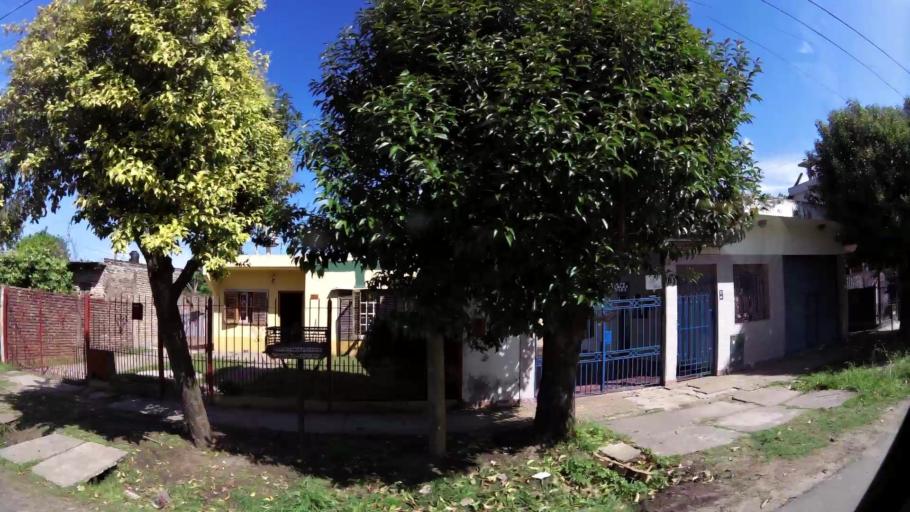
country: AR
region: Buenos Aires
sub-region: Partido de Quilmes
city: Quilmes
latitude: -34.8005
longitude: -58.2542
